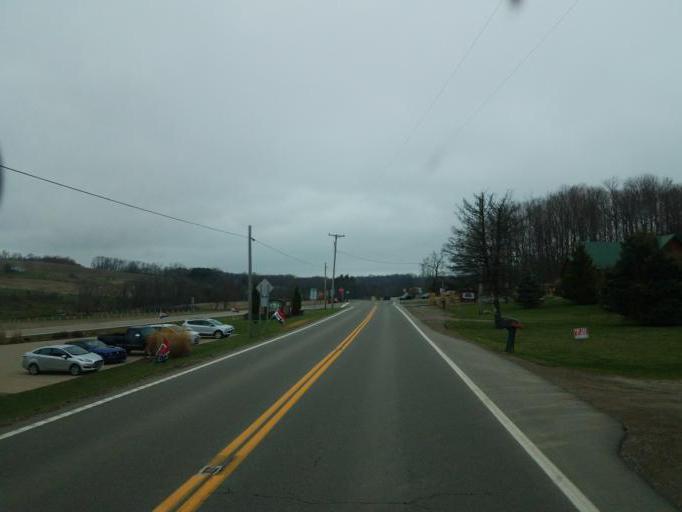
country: US
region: Ohio
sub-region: Ashland County
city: Loudonville
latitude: 40.7051
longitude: -82.2436
